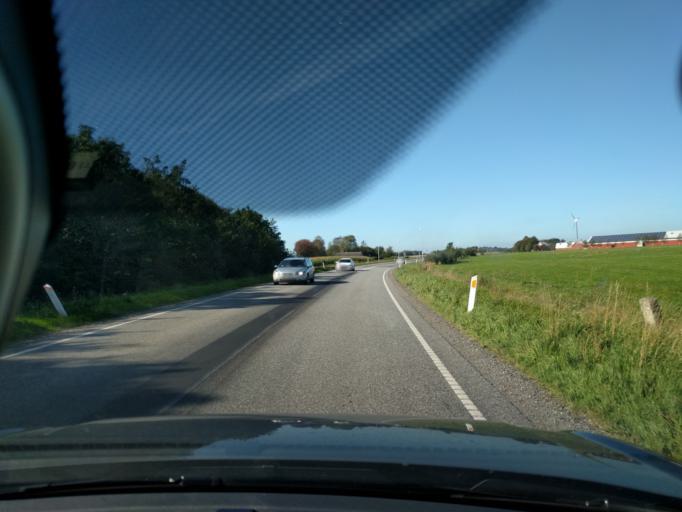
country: DK
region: North Denmark
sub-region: Mariagerfjord Kommune
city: Hobro
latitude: 56.6791
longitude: 9.6647
